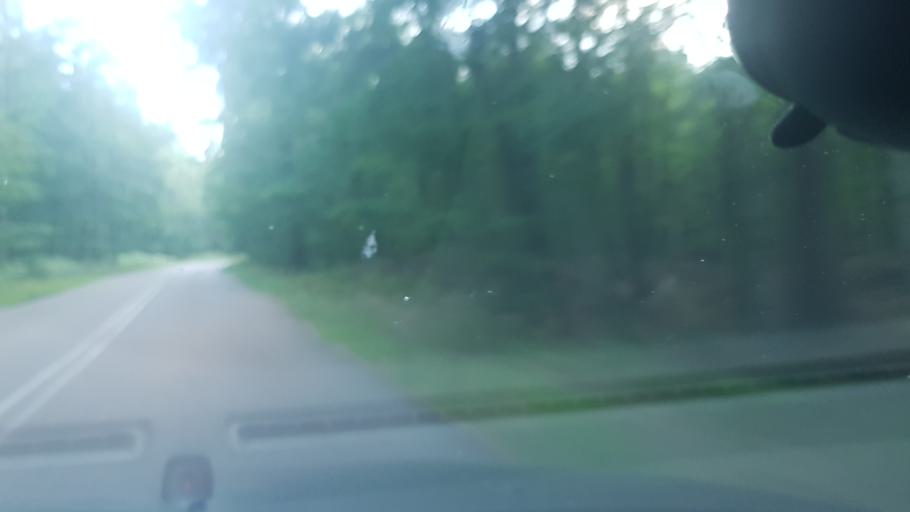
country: PL
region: Pomeranian Voivodeship
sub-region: Powiat nowodworski
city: Krynica Morska
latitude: 54.3578
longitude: 19.3329
